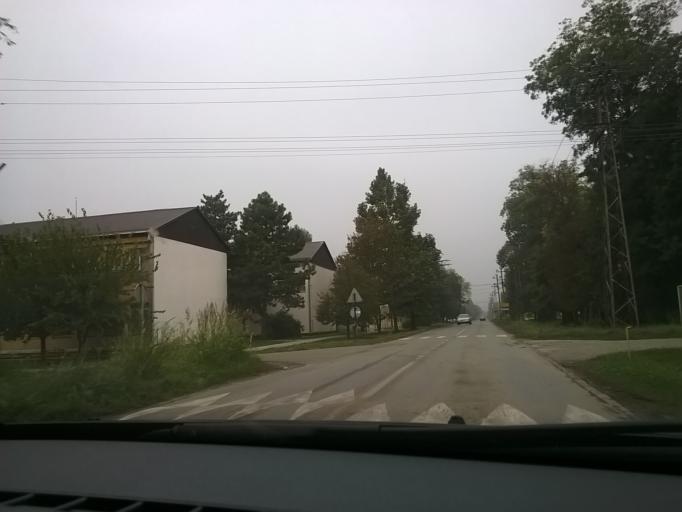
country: RS
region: Autonomna Pokrajina Vojvodina
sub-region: Juznobanatski Okrug
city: Kovin
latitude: 44.8783
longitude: 20.9735
